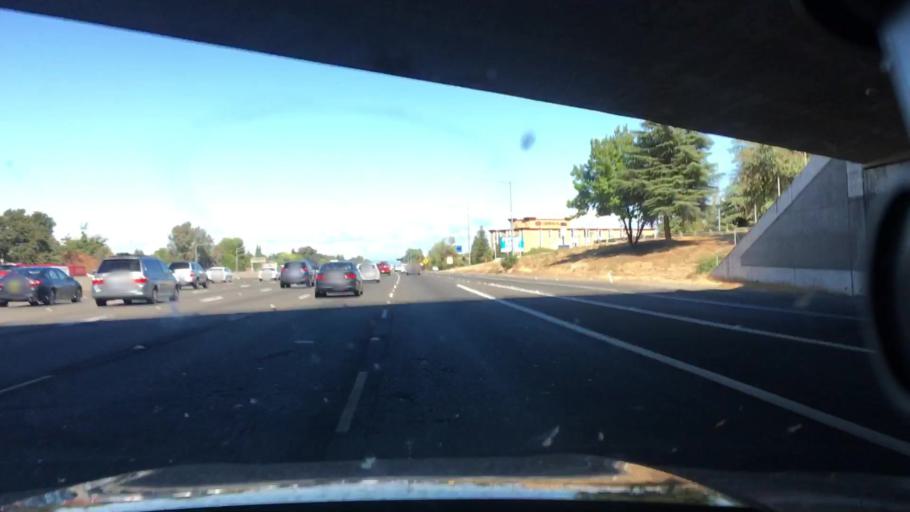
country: US
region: California
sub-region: Sacramento County
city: Foothill Farms
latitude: 38.6616
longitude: -121.3613
